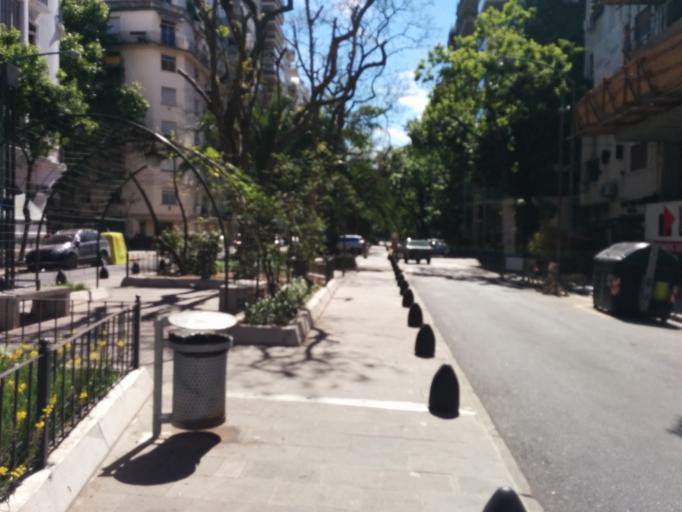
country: AR
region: Buenos Aires F.D.
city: Retiro
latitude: -34.5790
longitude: -58.4129
